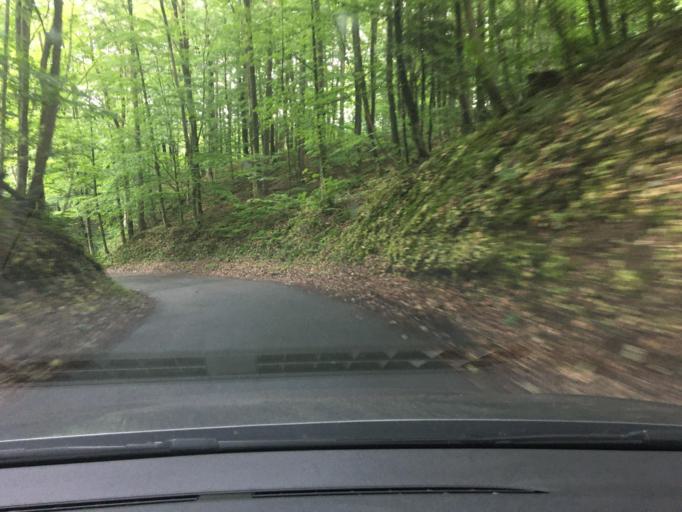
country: DK
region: South Denmark
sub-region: Fredericia Kommune
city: Taulov
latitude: 55.5522
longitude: 9.5358
